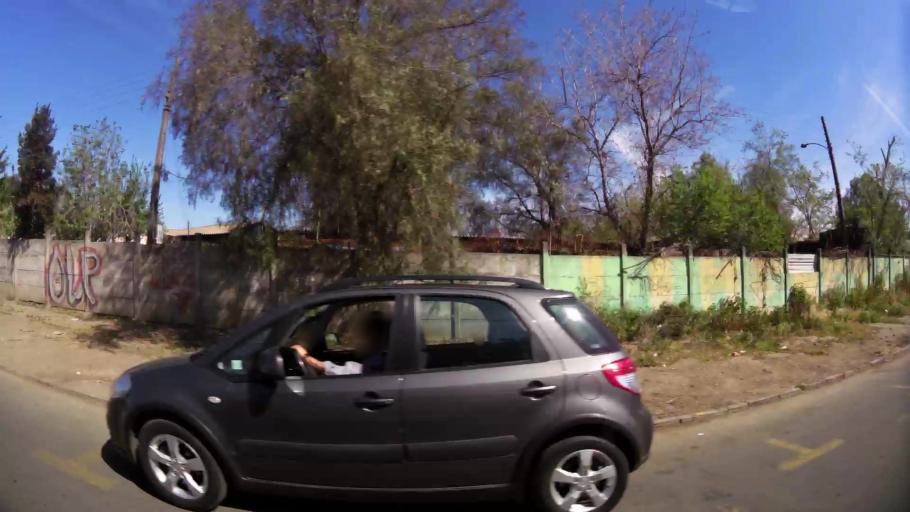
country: CL
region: Santiago Metropolitan
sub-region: Provincia de Santiago
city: Lo Prado
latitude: -33.4946
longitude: -70.7153
